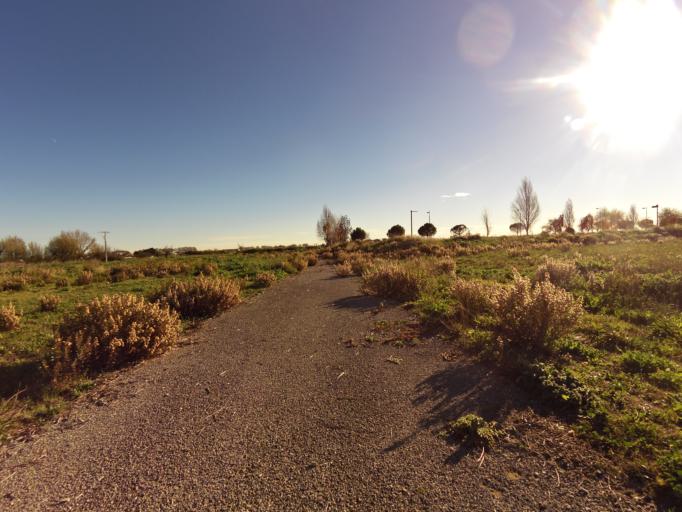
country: FR
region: Languedoc-Roussillon
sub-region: Departement du Gard
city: Aigues-Vives
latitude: 43.7206
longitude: 4.1912
